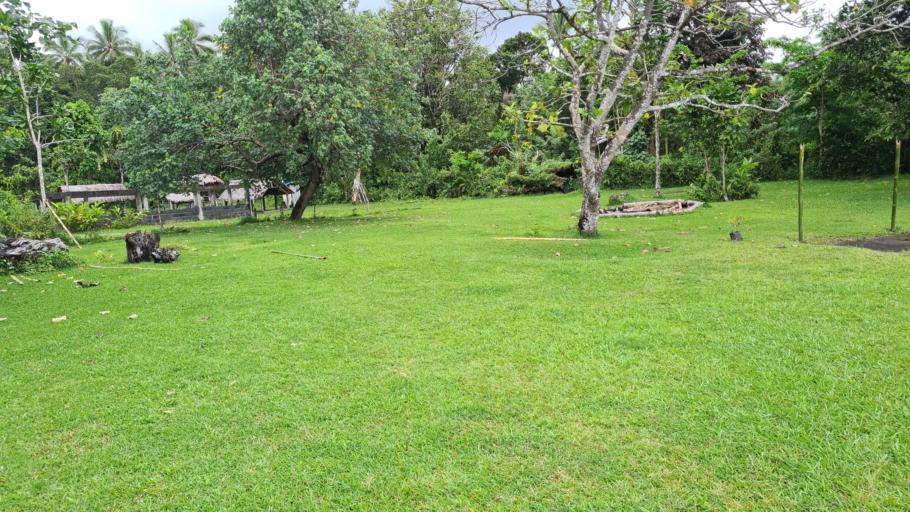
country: VU
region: Malampa
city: Lakatoro
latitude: -16.2595
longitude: 168.2539
